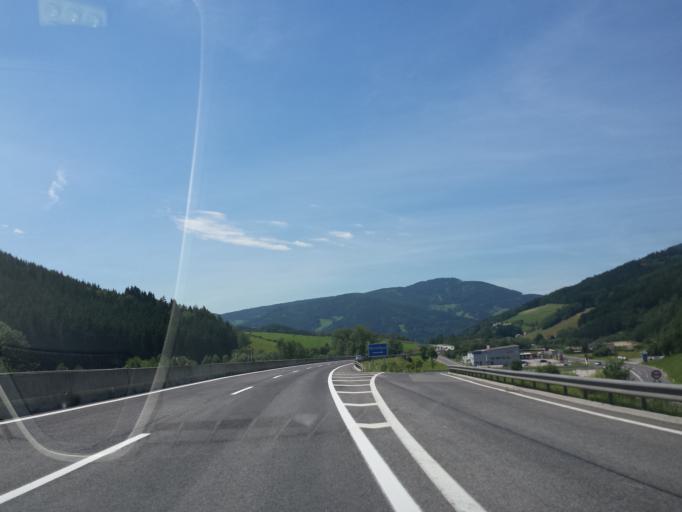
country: AT
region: Styria
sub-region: Politischer Bezirk Bruck-Muerzzuschlag
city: Spital am Semmering
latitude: 47.6009
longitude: 15.7242
